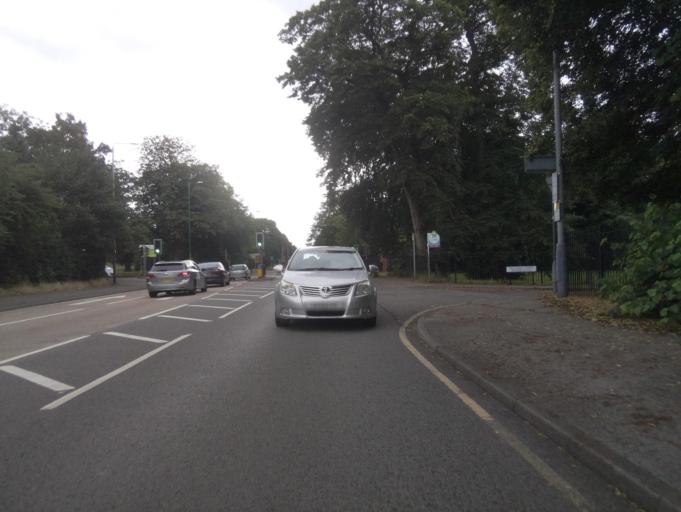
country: GB
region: England
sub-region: Nottinghamshire
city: Arnold
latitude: 52.9867
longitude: -1.1422
